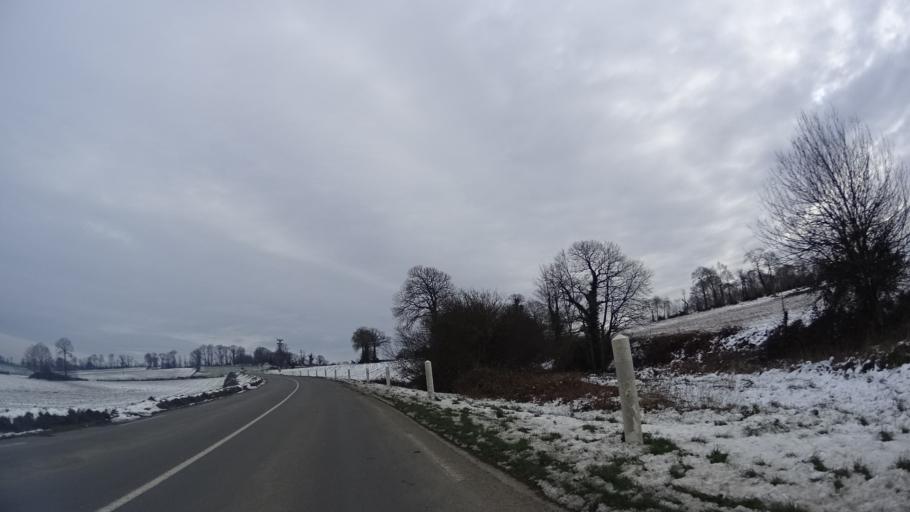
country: FR
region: Brittany
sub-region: Departement d'Ille-et-Vilaine
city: Irodouer
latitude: 48.3057
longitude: -1.9459
